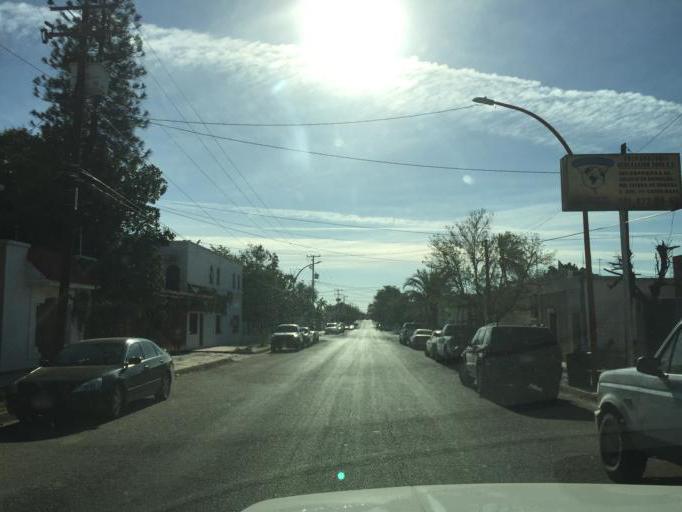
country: MX
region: Sonora
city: Navojoa
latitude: 27.0834
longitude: -109.4482
